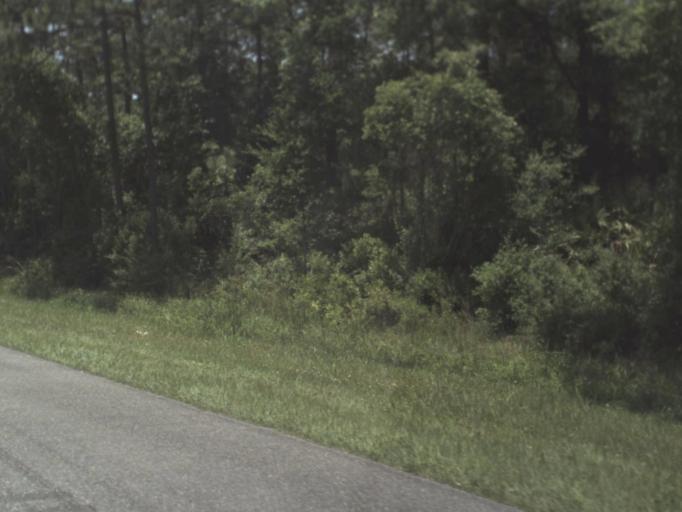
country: US
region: Florida
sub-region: Columbia County
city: Watertown
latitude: 30.2468
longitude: -82.5543
